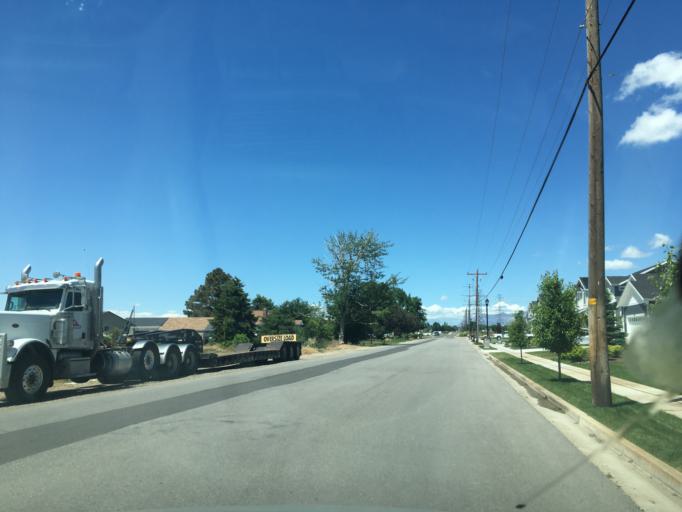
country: US
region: Utah
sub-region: Davis County
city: Layton
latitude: 41.0509
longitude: -112.0070
